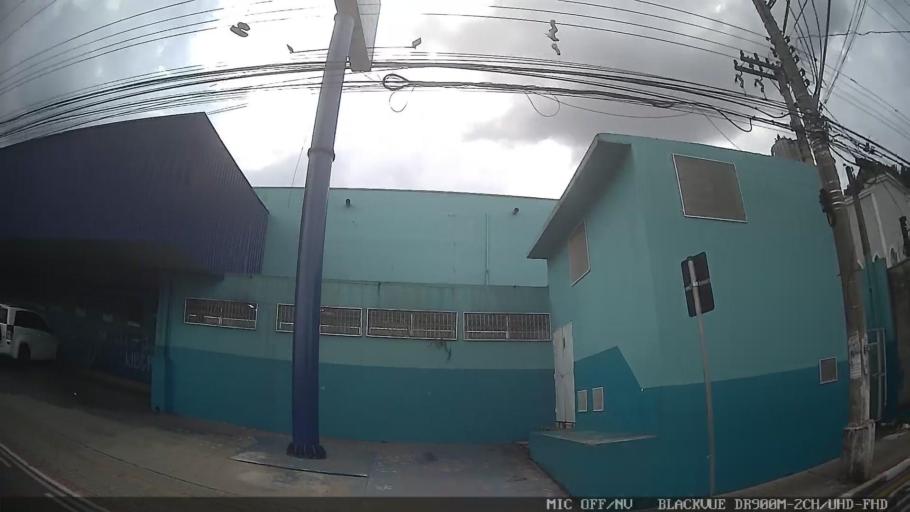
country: BR
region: Sao Paulo
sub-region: Poa
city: Poa
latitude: -23.5341
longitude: -46.3392
